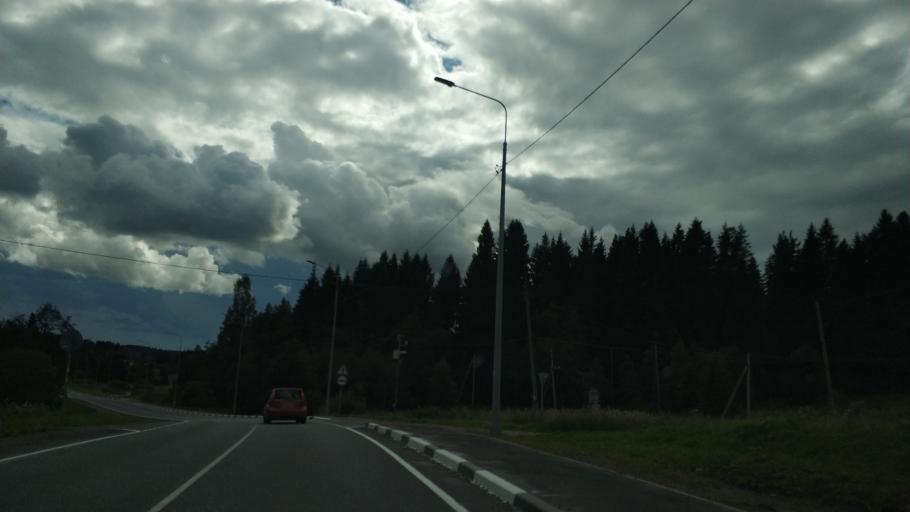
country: RU
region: Republic of Karelia
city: Khelyulya
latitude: 61.7681
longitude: 30.6541
